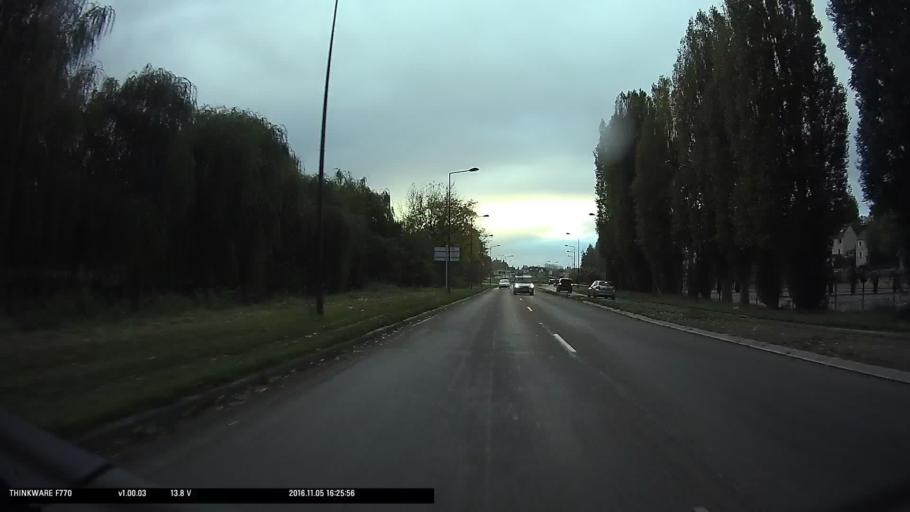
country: FR
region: Ile-de-France
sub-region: Departement des Yvelines
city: Meulan-en-Yvelines
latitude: 49.0145
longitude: 1.9099
